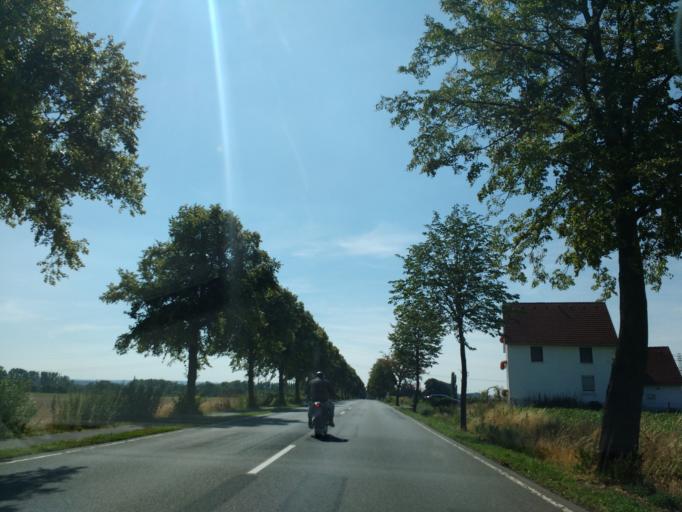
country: DE
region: Lower Saxony
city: Sohlde
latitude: 52.2241
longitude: 10.2294
